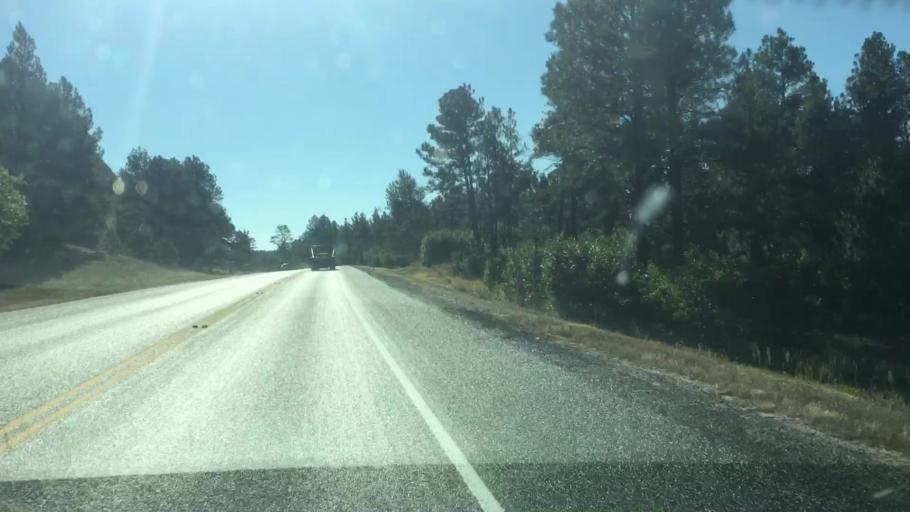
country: US
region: Colorado
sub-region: Douglas County
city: The Pinery
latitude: 39.3819
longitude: -104.7237
